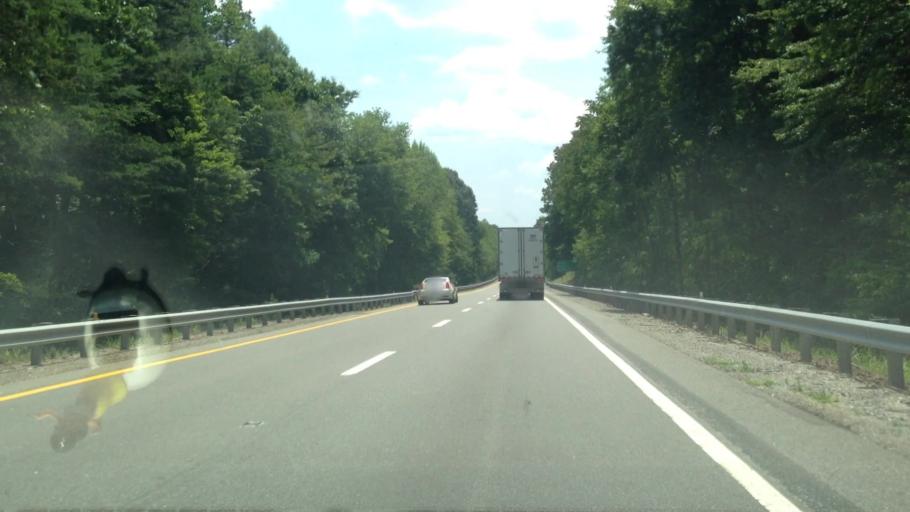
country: US
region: Virginia
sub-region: Henry County
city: Horse Pasture
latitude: 36.6415
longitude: -79.8985
